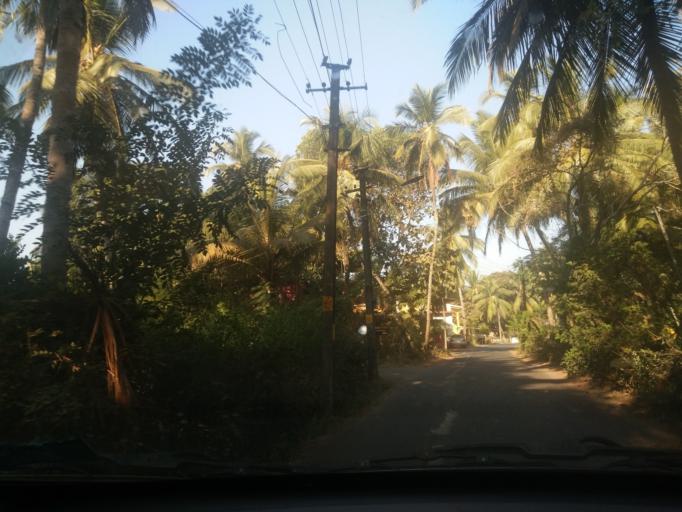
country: IN
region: Goa
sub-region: South Goa
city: Colva
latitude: 15.3023
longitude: 73.9158
